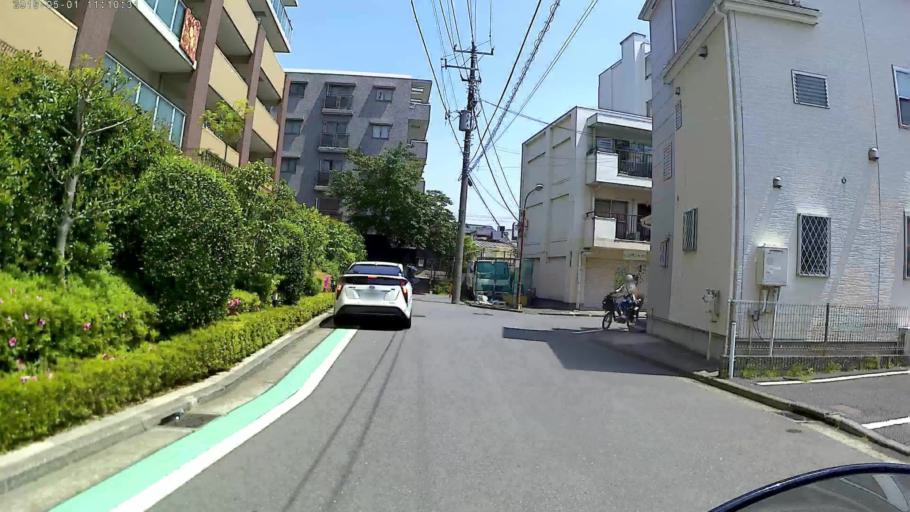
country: JP
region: Kanagawa
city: Minami-rinkan
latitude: 35.4880
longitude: 139.5415
